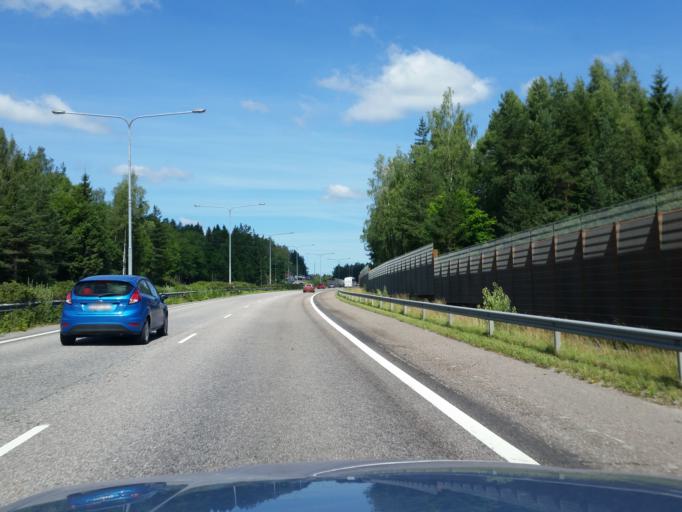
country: FI
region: Uusimaa
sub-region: Helsinki
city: Espoo
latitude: 60.2342
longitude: 24.5838
